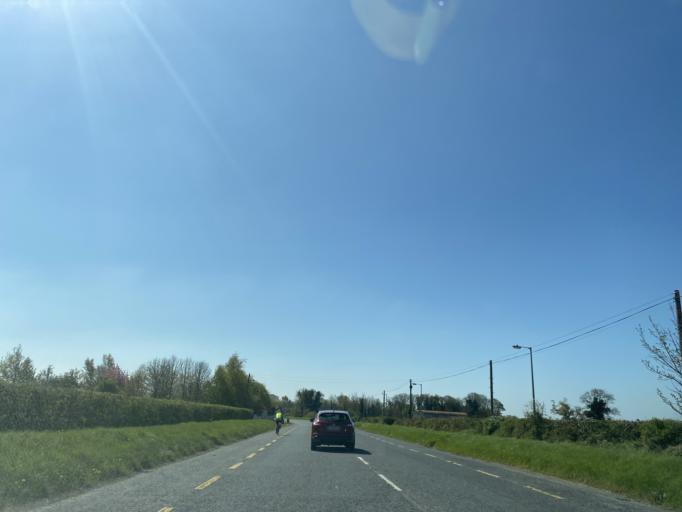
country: IE
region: Leinster
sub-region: Kildare
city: Maynooth
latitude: 53.3271
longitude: -6.6079
